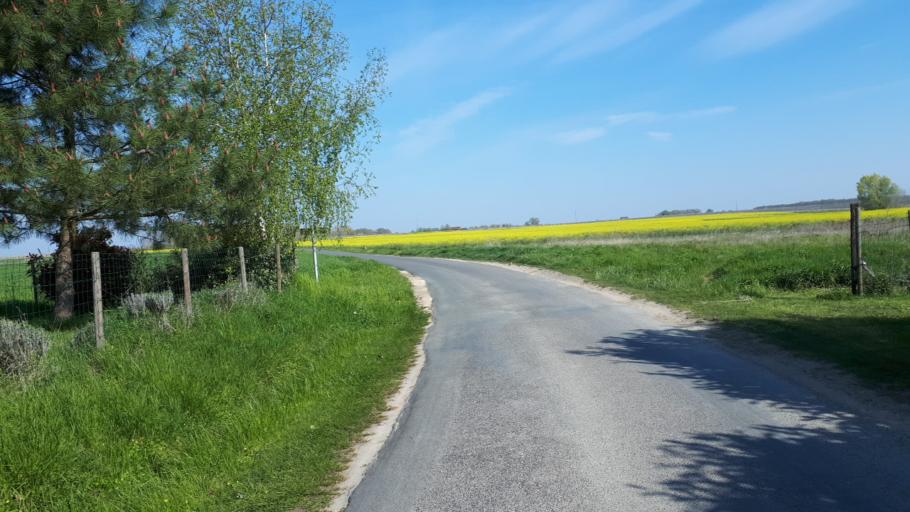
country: FR
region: Centre
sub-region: Departement du Loir-et-Cher
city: Contres
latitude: 47.3834
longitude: 1.3898
